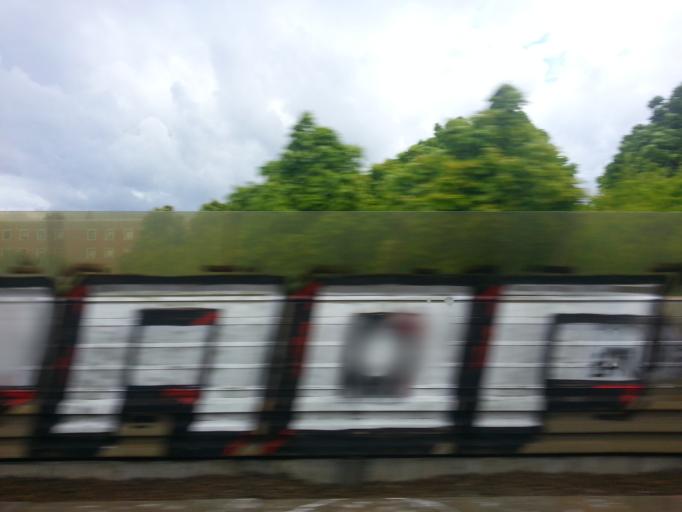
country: NO
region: Akershus
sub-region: Skedsmo
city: Lillestrom
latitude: 59.9598
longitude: 11.0621
